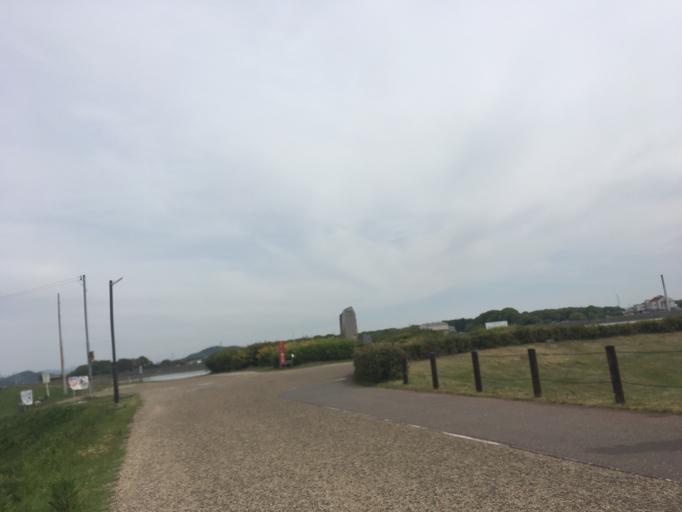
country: JP
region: Hyogo
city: Miki
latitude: 34.7671
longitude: 134.9212
